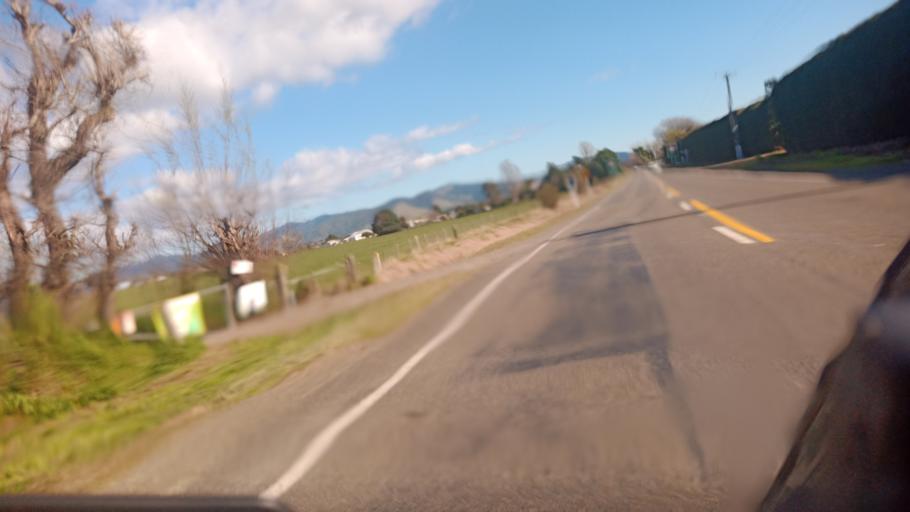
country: NZ
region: Bay of Plenty
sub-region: Opotiki District
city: Opotiki
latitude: -38.0017
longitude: 177.2967
